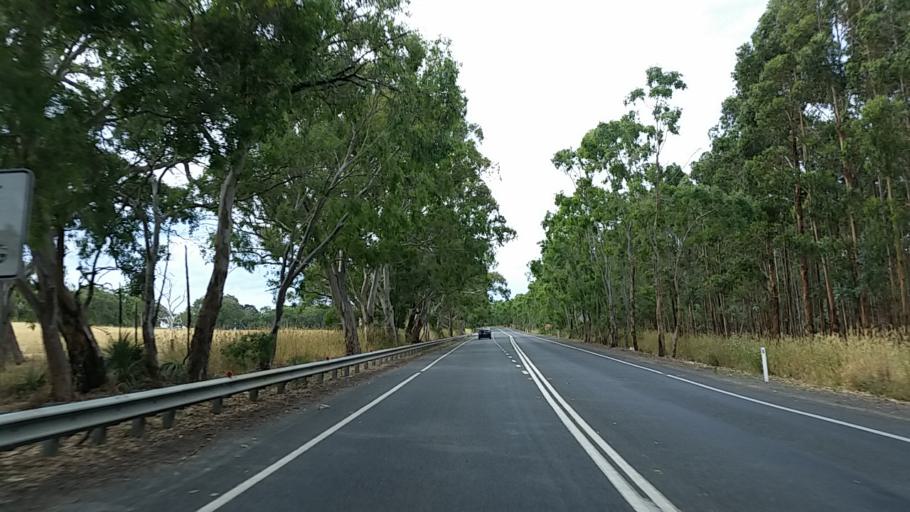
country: AU
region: South Australia
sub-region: Onkaparinga
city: Aldinga
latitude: -35.3757
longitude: 138.4648
